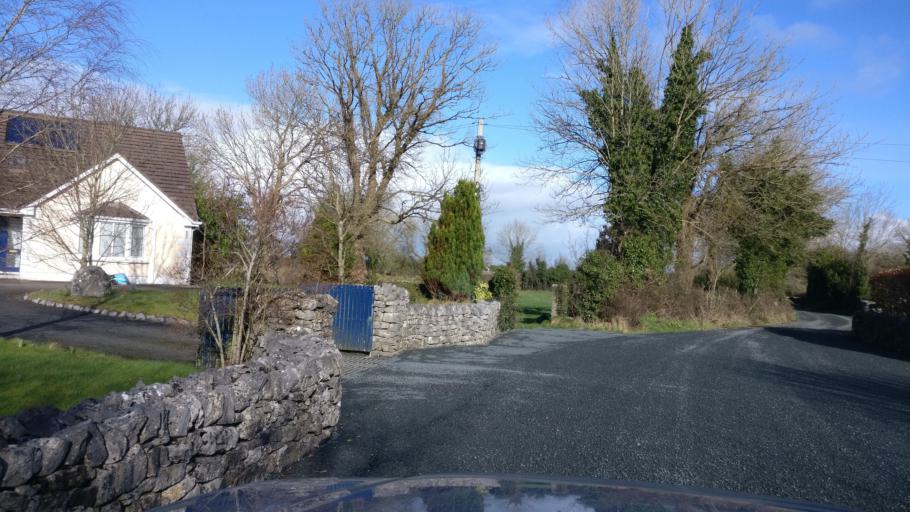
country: IE
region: Connaught
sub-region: County Galway
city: Athenry
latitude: 53.2329
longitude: -8.7748
